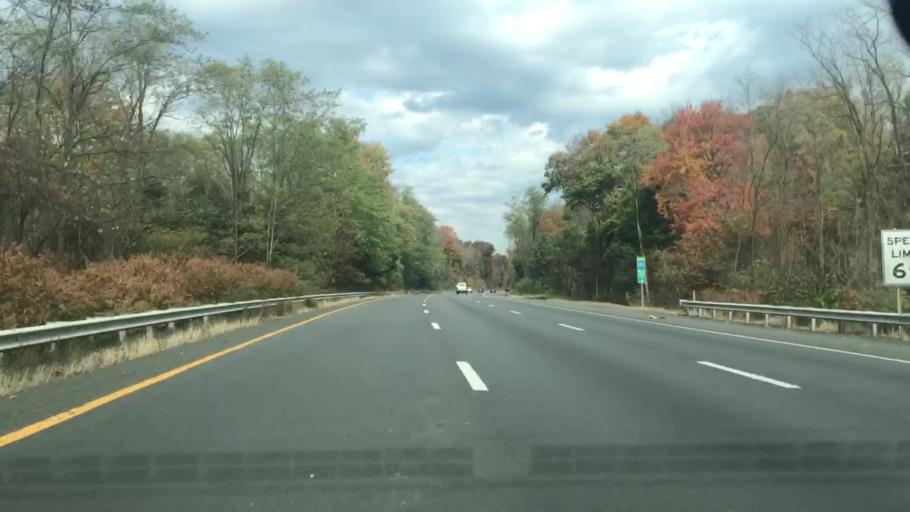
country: US
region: New Jersey
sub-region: Somerset County
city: Bernardsville
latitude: 40.7376
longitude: -74.5356
